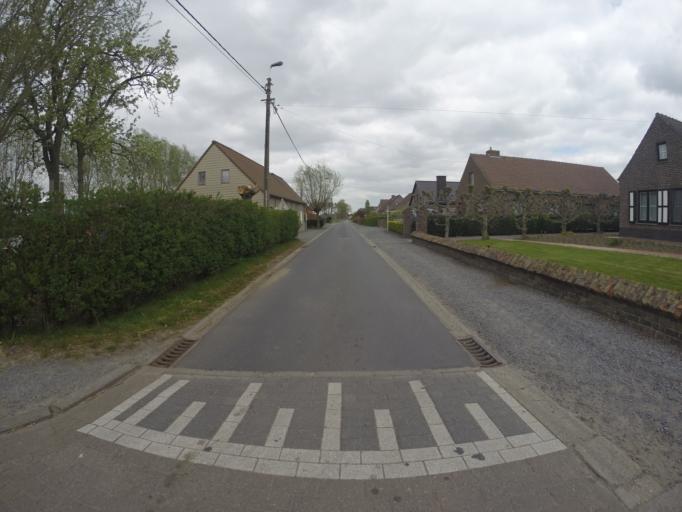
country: BE
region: Flanders
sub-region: Provincie Oost-Vlaanderen
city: Aalter
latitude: 51.0504
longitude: 3.4545
